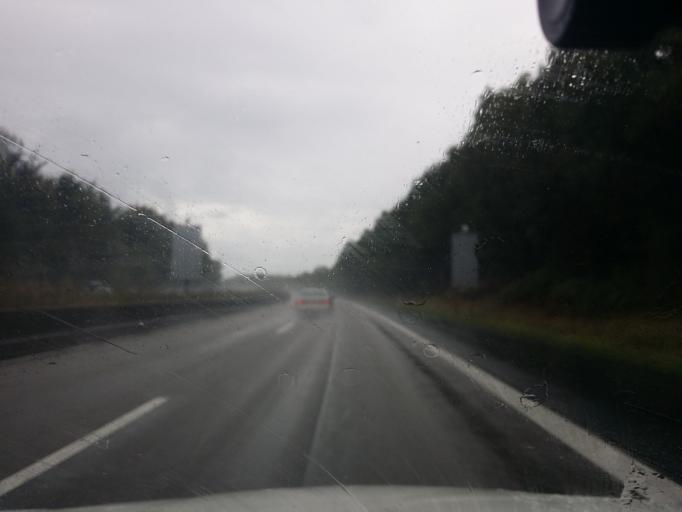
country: DE
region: Hesse
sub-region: Regierungsbezirk Kassel
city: Petersberg
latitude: 50.6138
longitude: 9.6828
